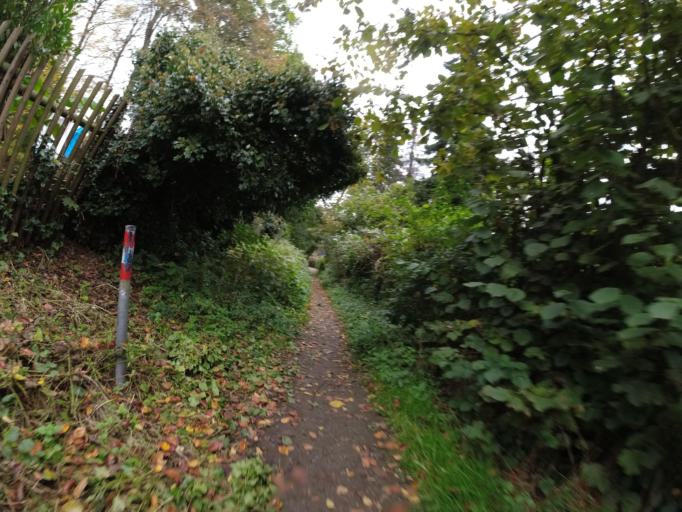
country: DE
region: North Rhine-Westphalia
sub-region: Regierungsbezirk Dusseldorf
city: Hochfeld
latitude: 51.4155
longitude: 6.6886
